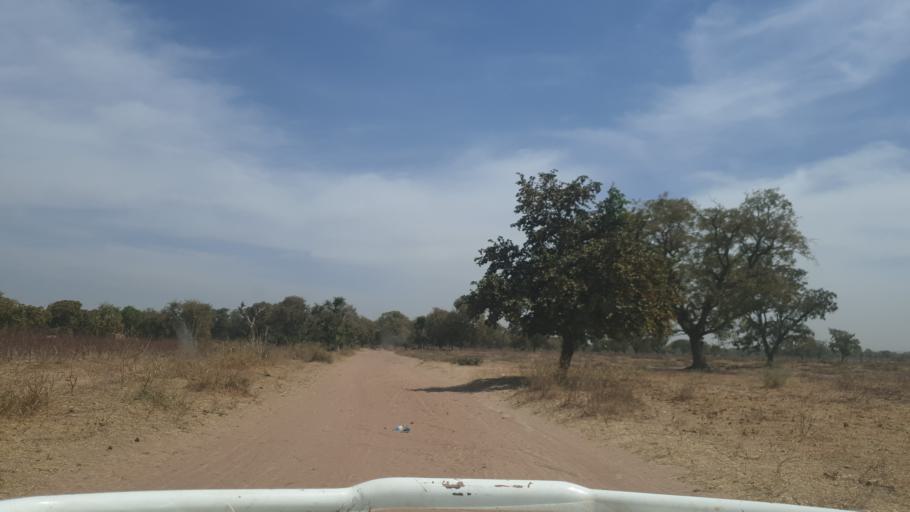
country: ML
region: Sikasso
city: Yorosso
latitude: 12.2953
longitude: -4.6415
